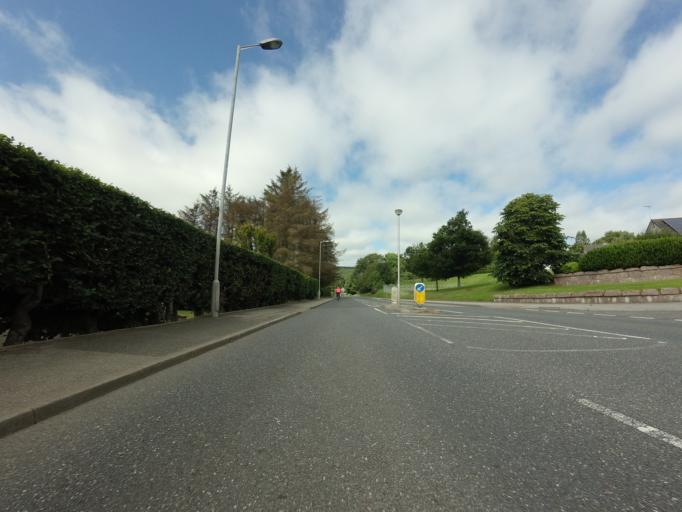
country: GB
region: Scotland
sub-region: Aberdeenshire
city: Turriff
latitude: 57.5422
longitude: -2.4746
